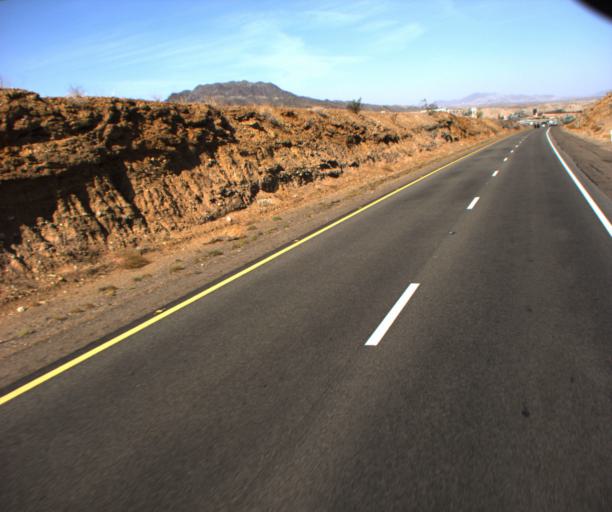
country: US
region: Arizona
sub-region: Mohave County
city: Desert Hills
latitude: 34.7186
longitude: -114.4685
